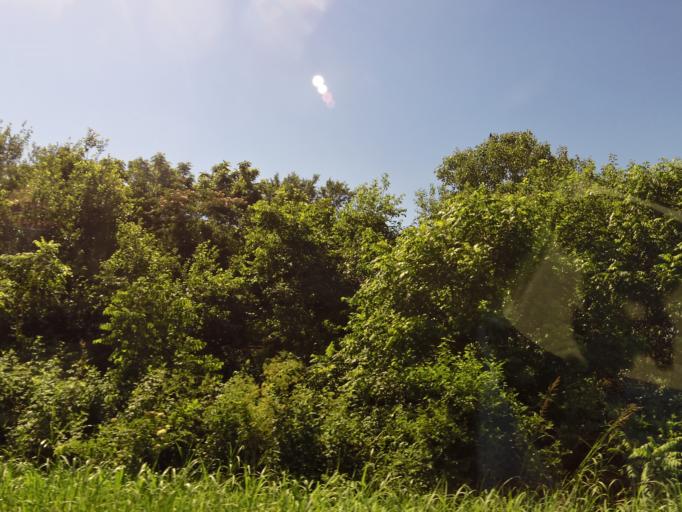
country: US
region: Missouri
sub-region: Dunklin County
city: Campbell
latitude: 36.4723
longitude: -90.1097
